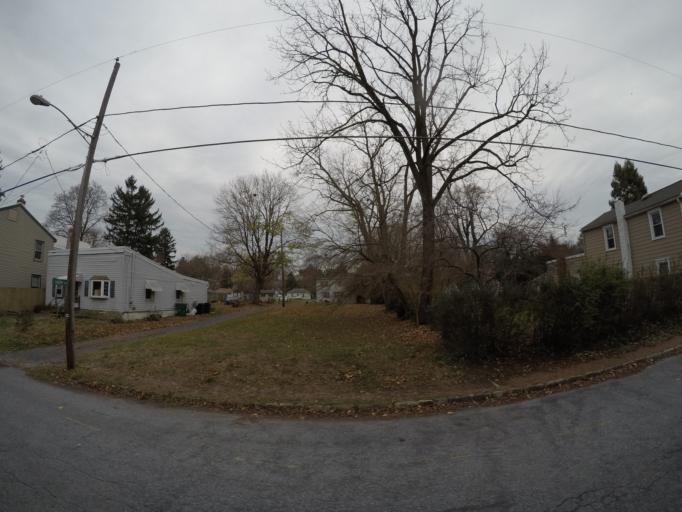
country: US
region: Pennsylvania
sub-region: Lancaster County
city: Marietta
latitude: 40.0566
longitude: -76.5492
